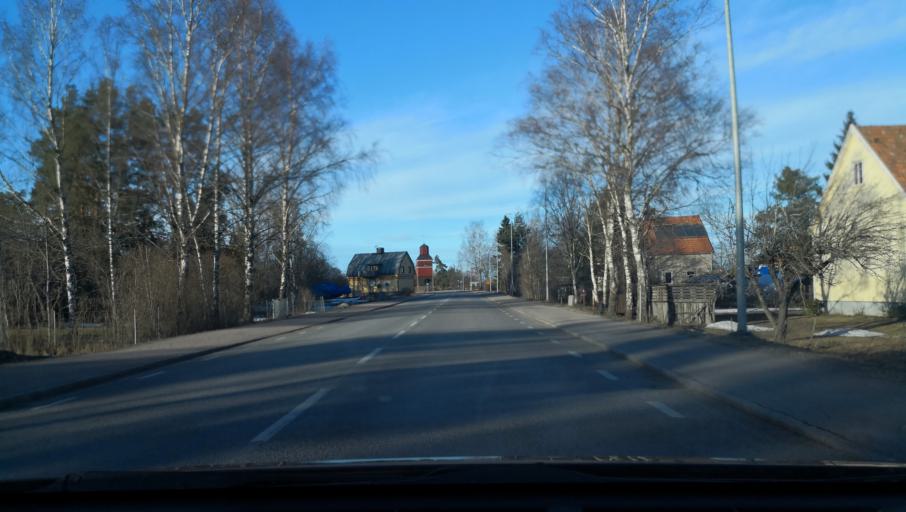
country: SE
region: Uppsala
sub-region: Osthammars Kommun
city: Gimo
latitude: 60.1701
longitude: 18.1937
